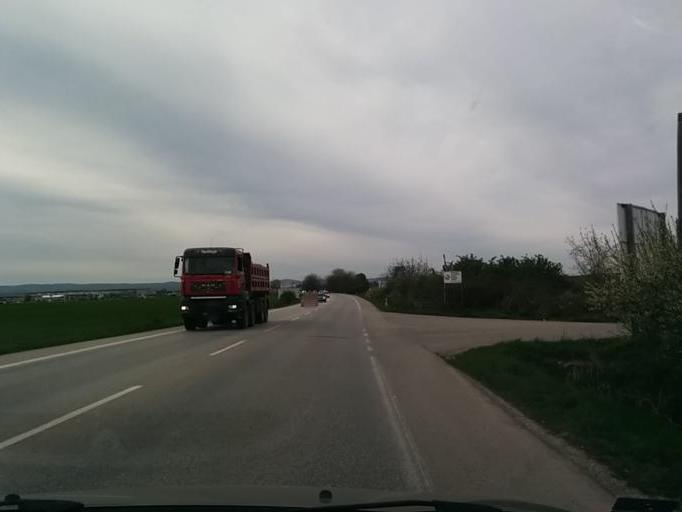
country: SK
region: Bratislavsky
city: Senec
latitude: 48.2263
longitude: 17.3808
